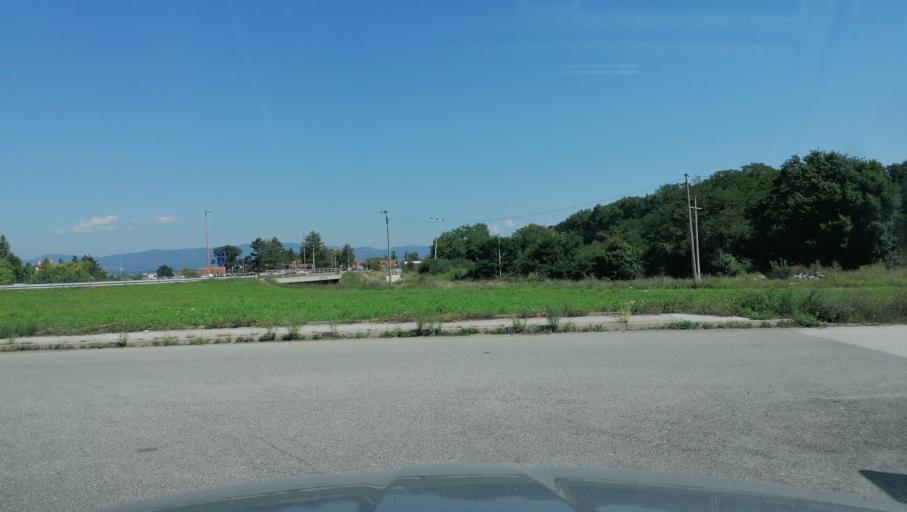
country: RS
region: Central Serbia
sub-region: Raski Okrug
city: Kraljevo
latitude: 43.6926
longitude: 20.6461
